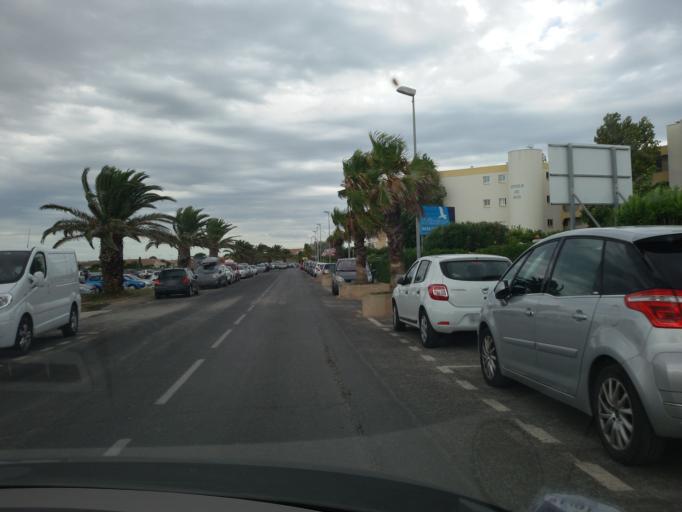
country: FR
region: Languedoc-Roussillon
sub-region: Departement de l'Herault
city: Palavas-les-Flots
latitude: 43.5218
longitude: 3.9160
